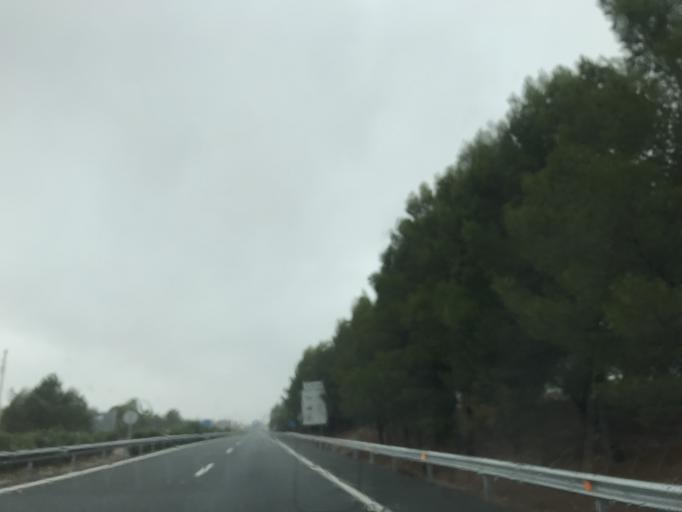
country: ES
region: Andalusia
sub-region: Provincia de Malaga
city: Fuente de Piedra
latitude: 37.1376
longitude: -4.7177
